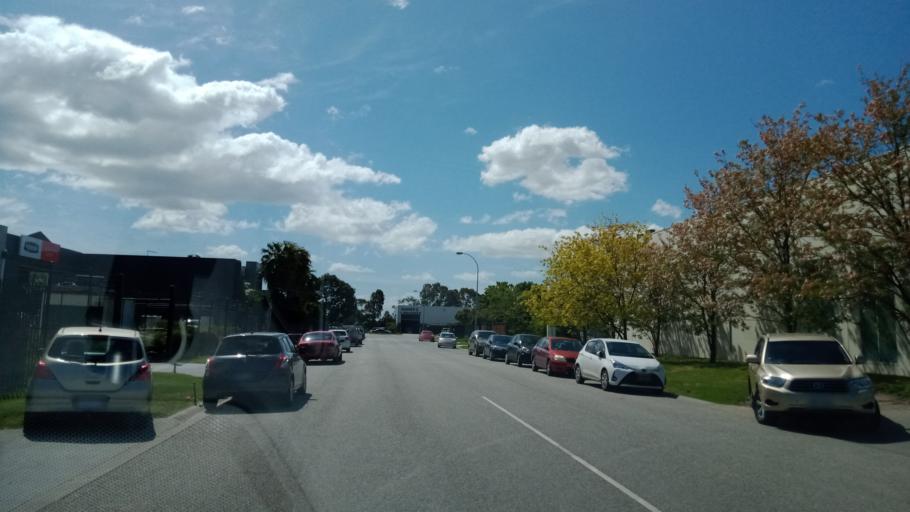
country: AU
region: Victoria
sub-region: Kingston
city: Chelsea Heights
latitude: -38.0357
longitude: 145.1357
